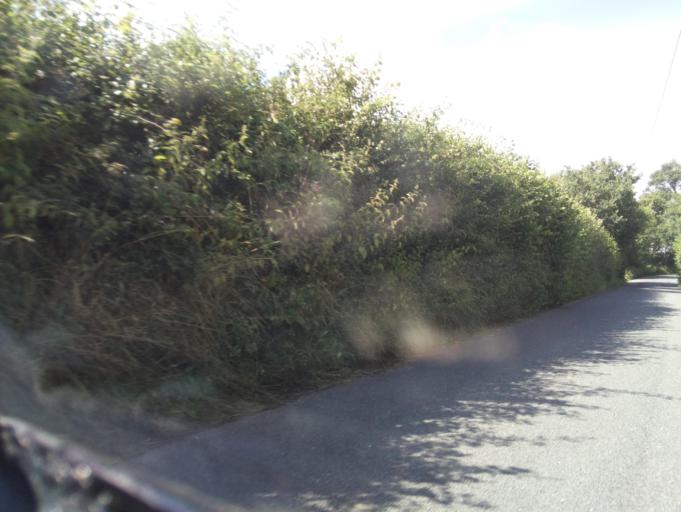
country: GB
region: England
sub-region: West Berkshire
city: Greenham
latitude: 51.3546
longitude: -1.2817
